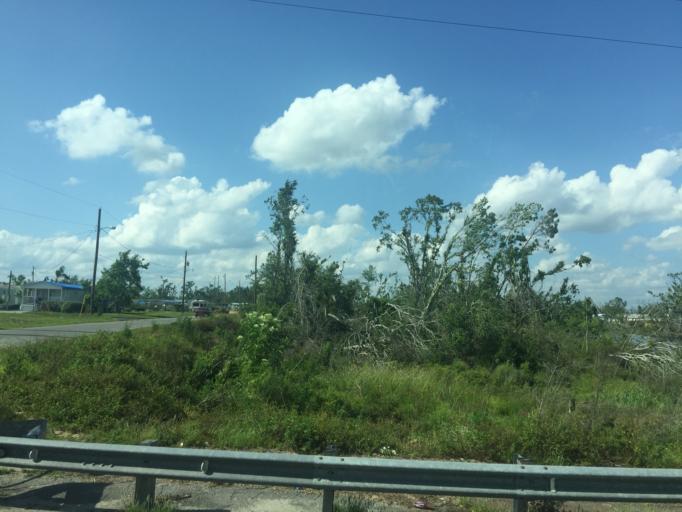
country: US
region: Florida
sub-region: Bay County
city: Springfield
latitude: 30.1604
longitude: -85.6035
